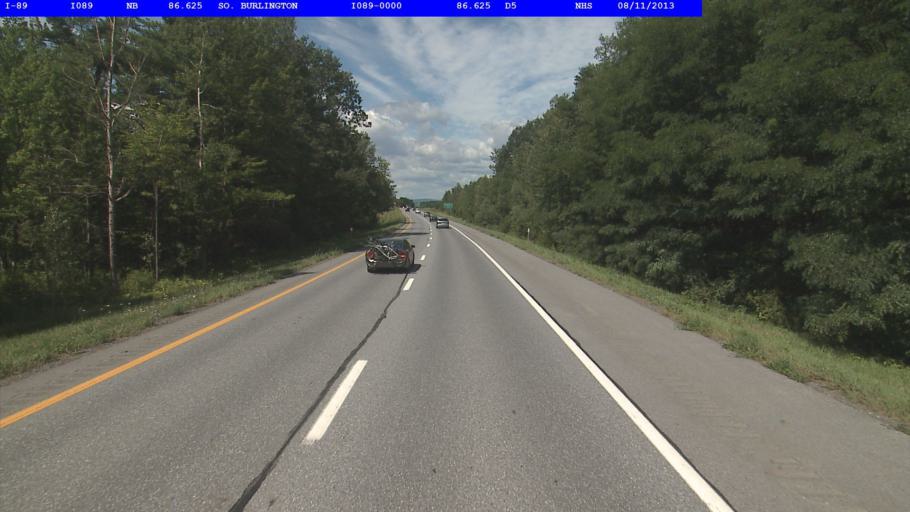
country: US
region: Vermont
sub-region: Chittenden County
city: South Burlington
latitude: 44.4496
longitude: -73.1665
